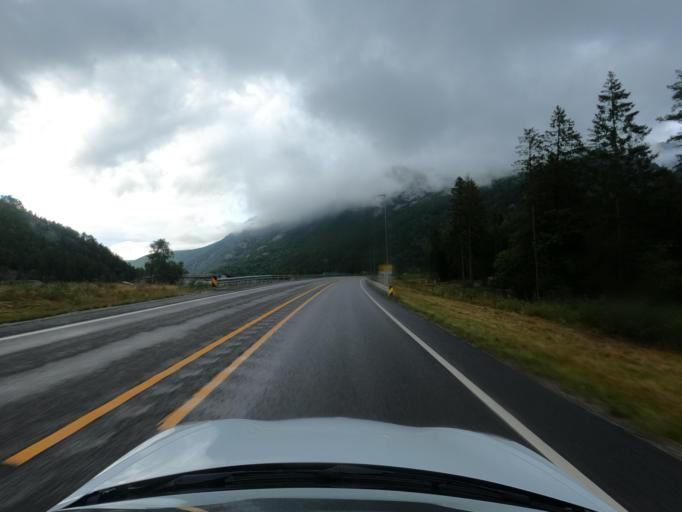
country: NO
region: Telemark
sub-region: Seljord
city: Seljord
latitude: 59.5143
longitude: 8.6481
